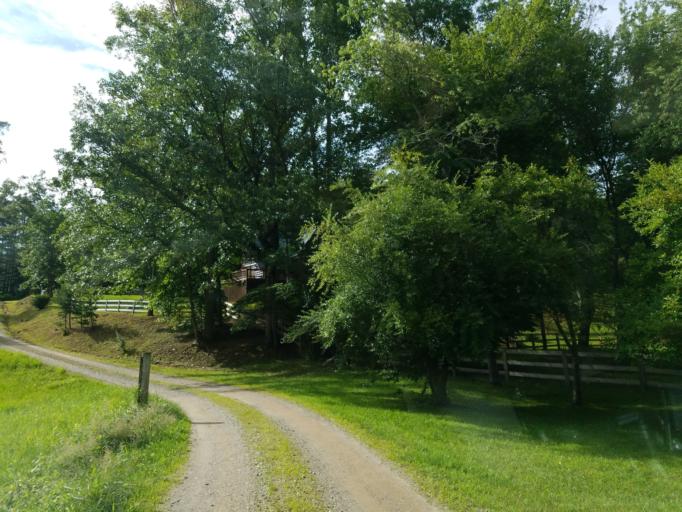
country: US
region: Georgia
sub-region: Union County
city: Blairsville
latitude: 34.7366
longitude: -84.0598
